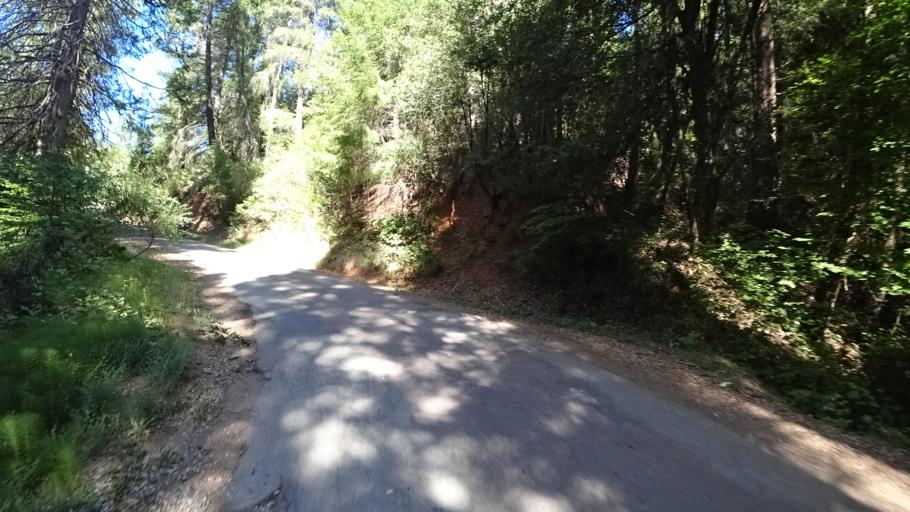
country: US
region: California
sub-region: Amador County
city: Pioneer
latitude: 38.3706
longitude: -120.4519
